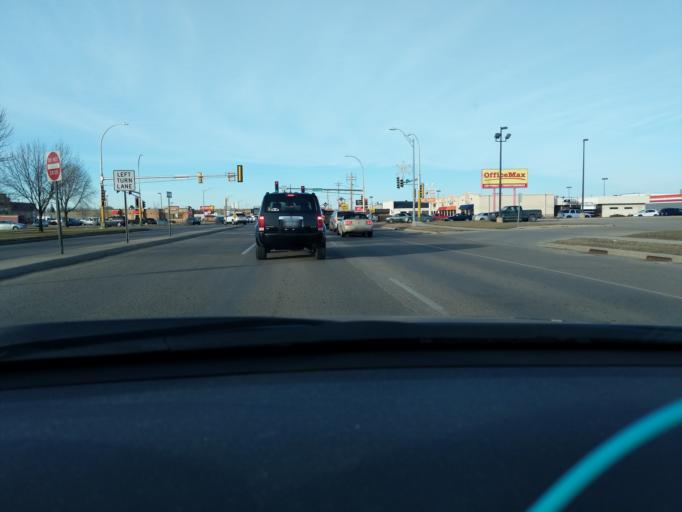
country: US
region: Minnesota
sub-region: Kandiyohi County
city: Willmar
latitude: 45.1026
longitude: -95.0426
